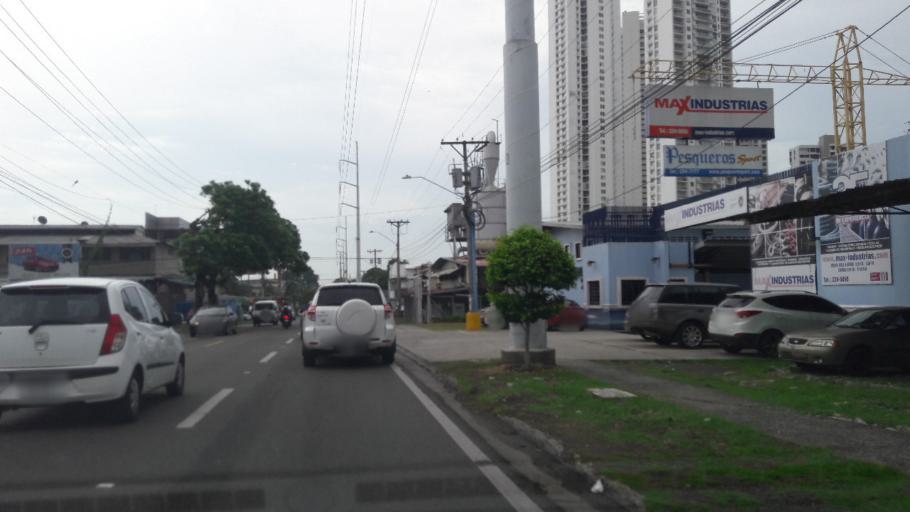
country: PA
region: Panama
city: Panama
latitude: 9.0055
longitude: -79.4977
